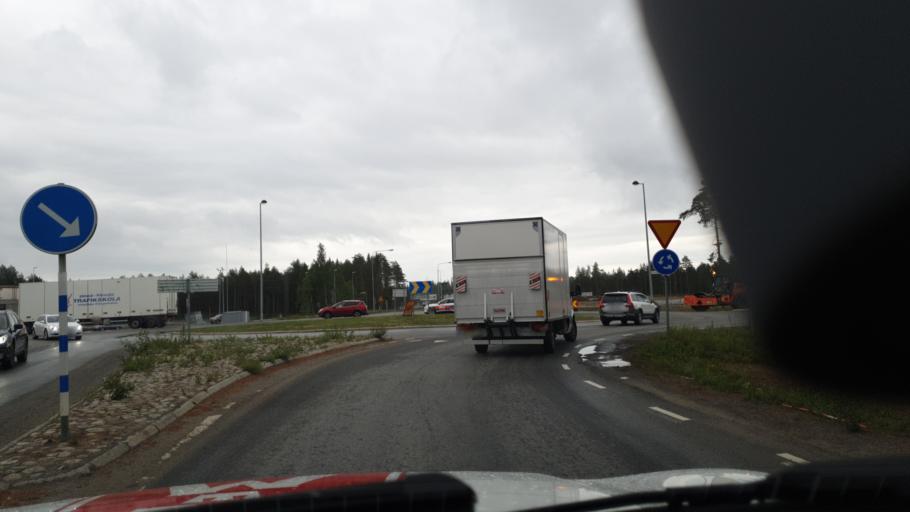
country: SE
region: Vaesterbotten
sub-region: Umea Kommun
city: Roback
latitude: 63.8475
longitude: 20.1589
